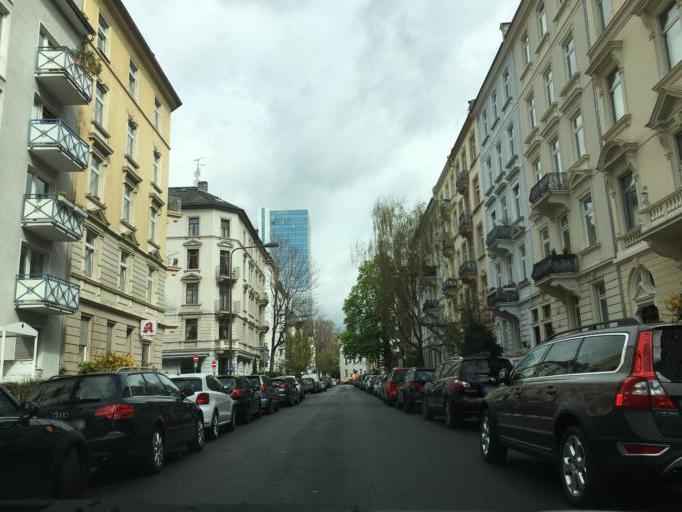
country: DE
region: Hesse
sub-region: Regierungsbezirk Darmstadt
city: Frankfurt am Main
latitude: 50.1207
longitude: 8.6676
